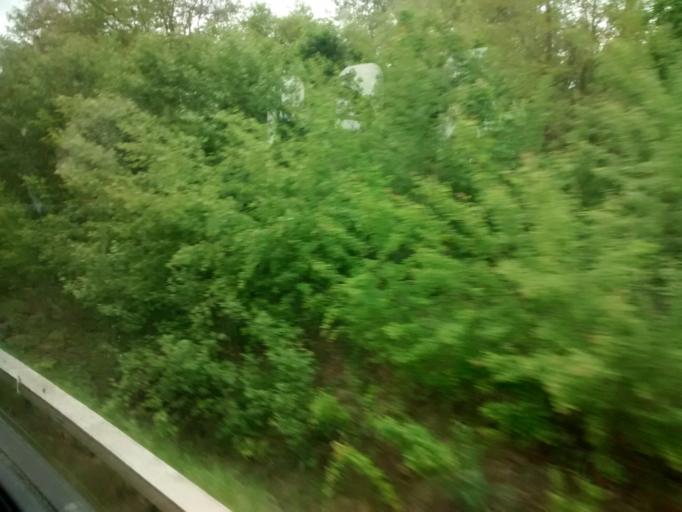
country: DE
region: Berlin
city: Blankenfelde
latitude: 52.6455
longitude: 13.4042
